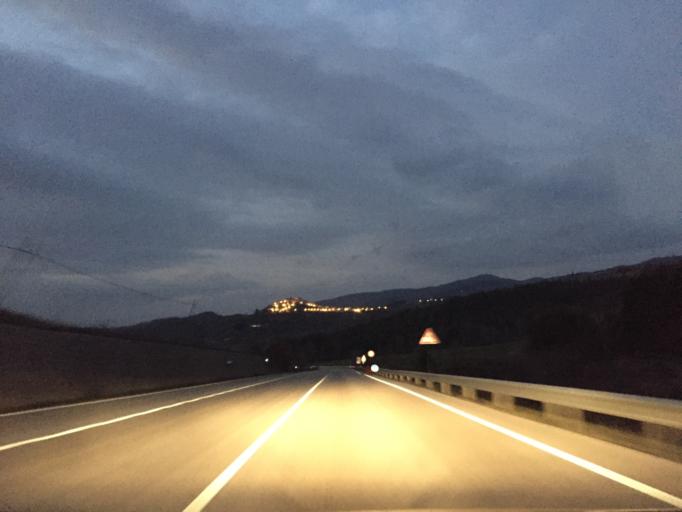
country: IT
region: Apulia
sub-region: Provincia di Foggia
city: Volturara Appula
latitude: 41.4771
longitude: 15.0536
